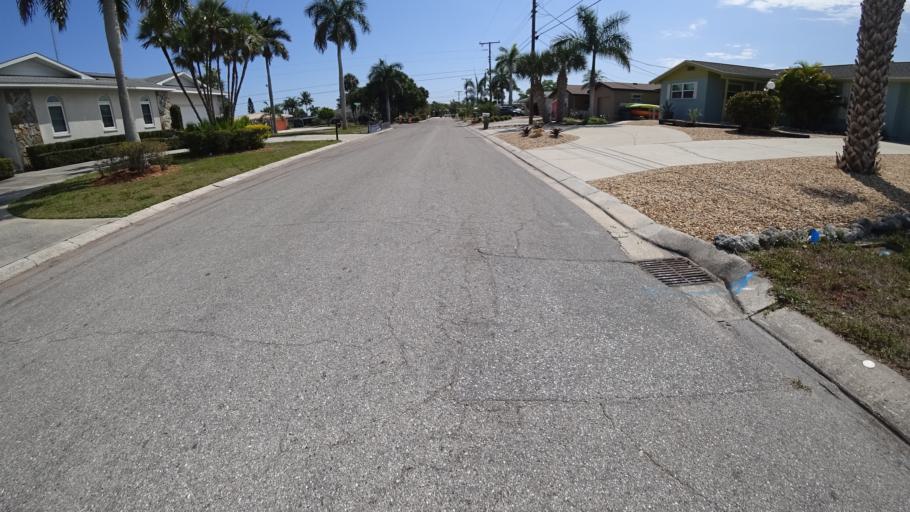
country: US
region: Florida
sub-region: Manatee County
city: Cortez
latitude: 27.4633
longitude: -82.6622
